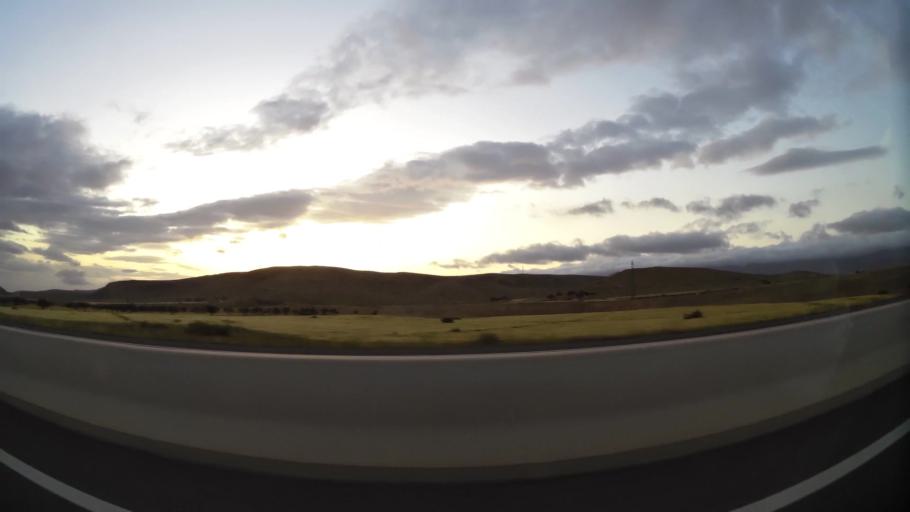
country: MA
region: Oriental
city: El Aioun
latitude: 34.6124
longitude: -2.5560
